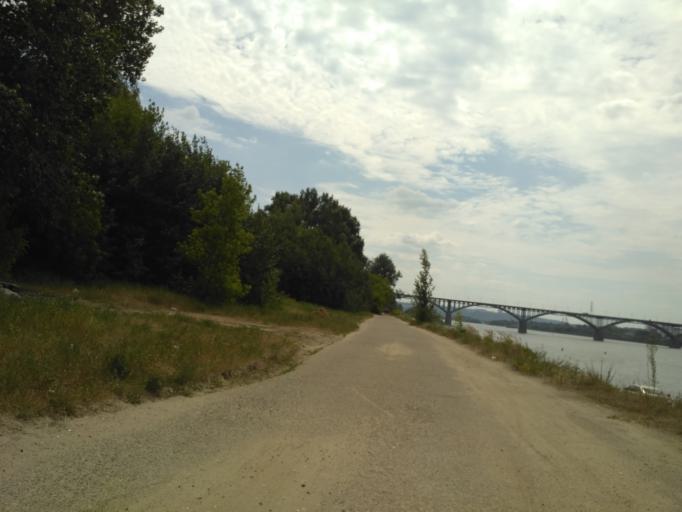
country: RU
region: Nizjnij Novgorod
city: Nizhniy Novgorod
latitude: 56.3088
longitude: 43.9681
